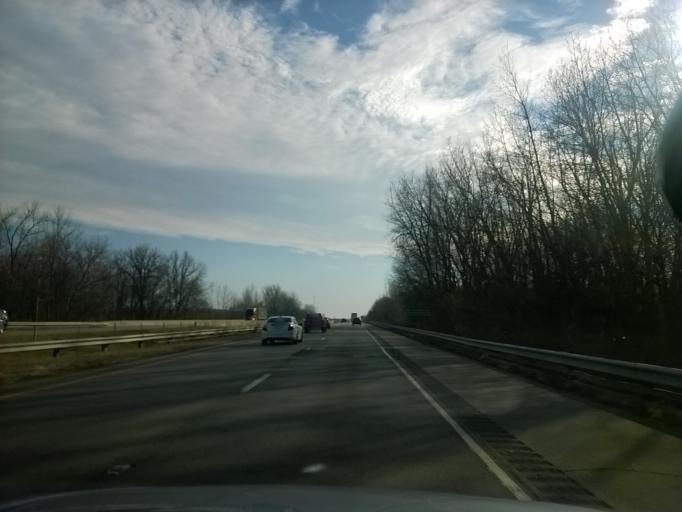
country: US
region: Indiana
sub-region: Johnson County
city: Edinburgh
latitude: 39.3933
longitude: -85.9432
